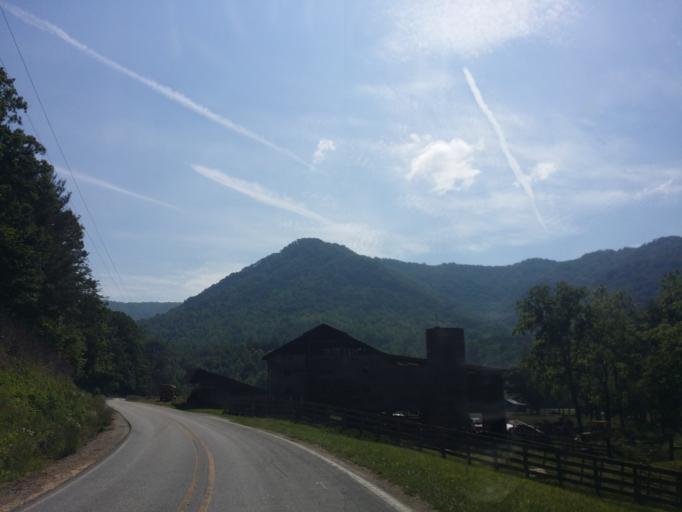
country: US
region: North Carolina
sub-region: Madison County
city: Marshall
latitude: 35.7724
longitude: -82.8791
